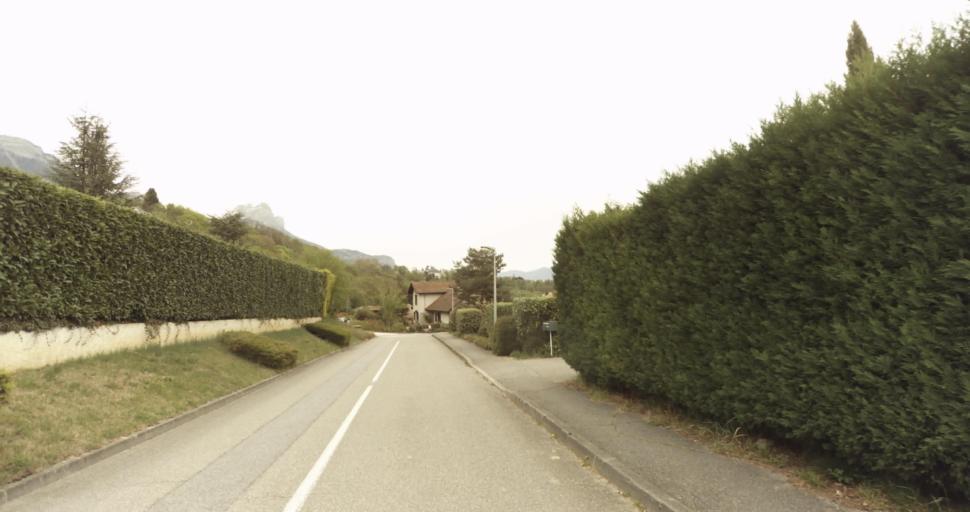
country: FR
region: Rhone-Alpes
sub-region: Departement de l'Isere
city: Montbonnot-Saint-Martin
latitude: 45.2298
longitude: 5.8134
